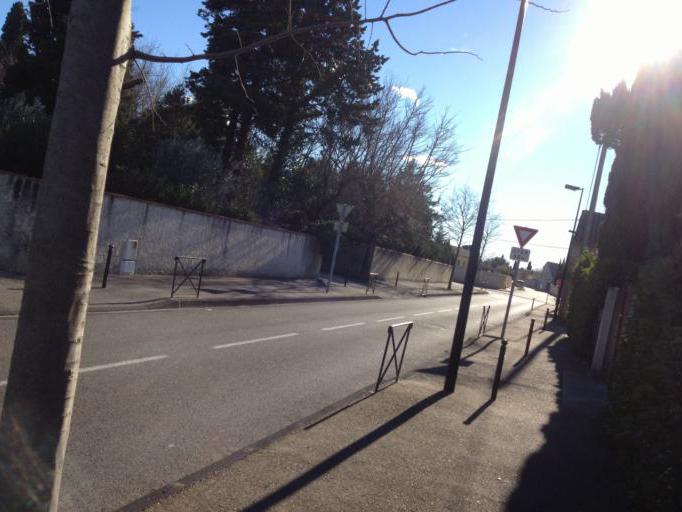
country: FR
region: Provence-Alpes-Cote d'Azur
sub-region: Departement du Vaucluse
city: Orange
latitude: 44.1490
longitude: 4.7991
